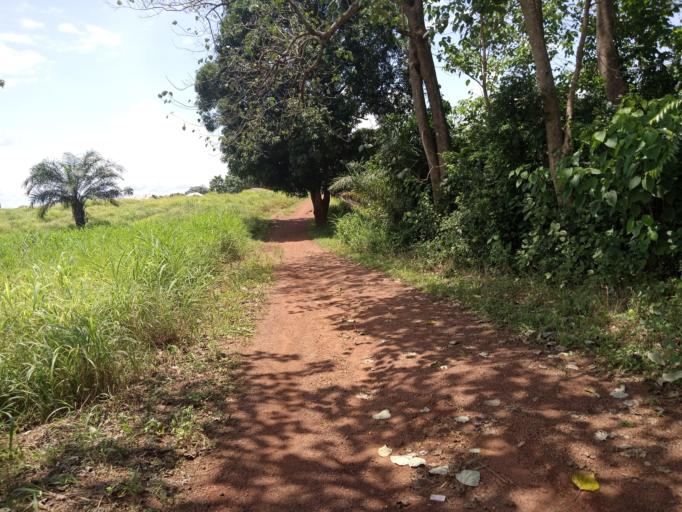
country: SL
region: Northern Province
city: Kamakwie
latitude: 9.4682
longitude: -12.2476
